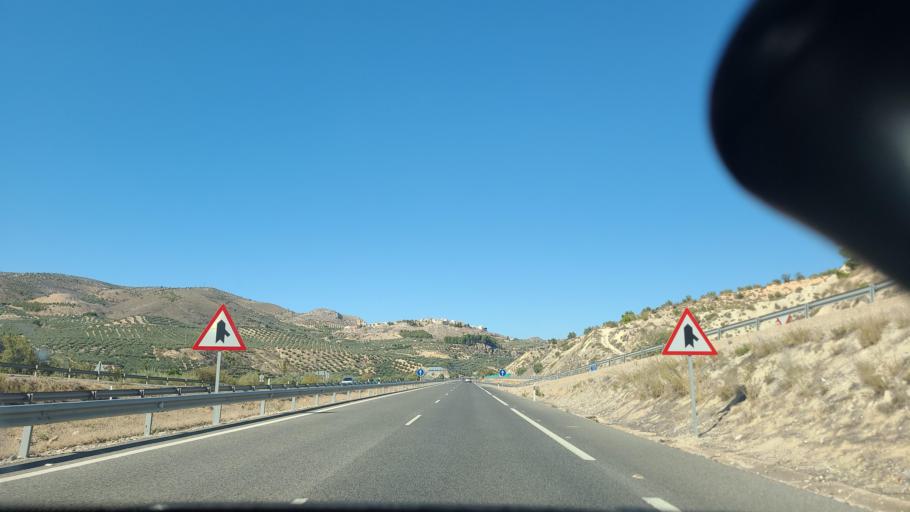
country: ES
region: Andalusia
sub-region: Provincia de Jaen
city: La Guardia de Jaen
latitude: 37.7266
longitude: -3.6802
